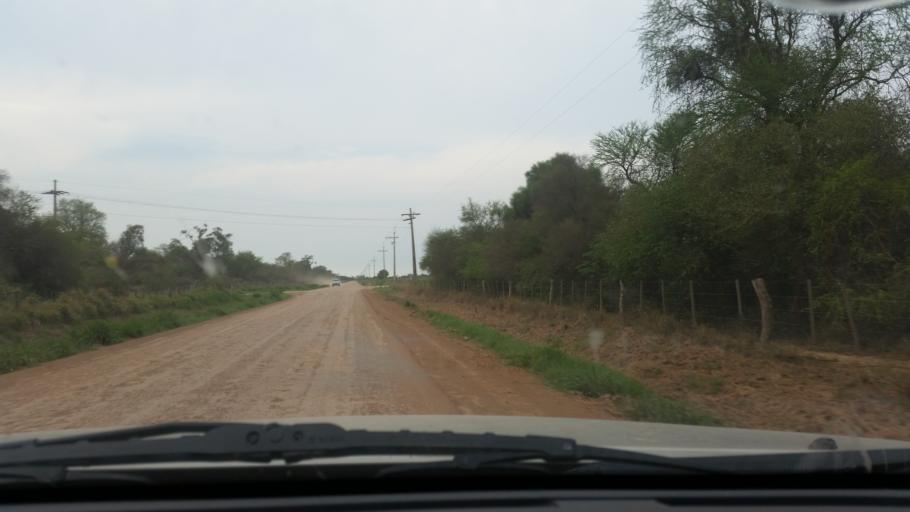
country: PY
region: Boqueron
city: Colonia Menno
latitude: -22.3500
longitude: -59.6223
